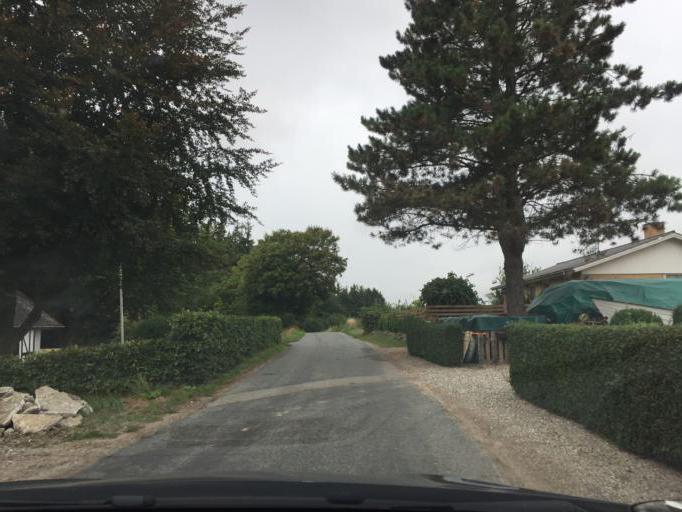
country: DK
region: South Denmark
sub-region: Assens Kommune
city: Harby
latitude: 55.1968
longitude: 10.0400
